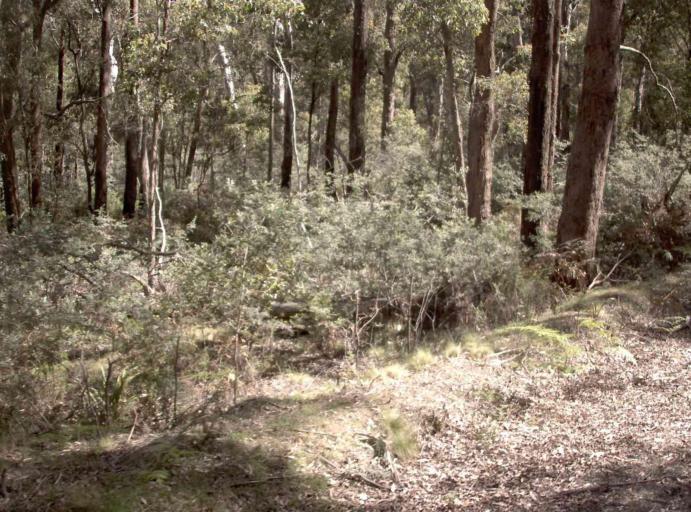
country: AU
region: New South Wales
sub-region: Bombala
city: Bombala
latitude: -37.1337
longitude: 148.7416
